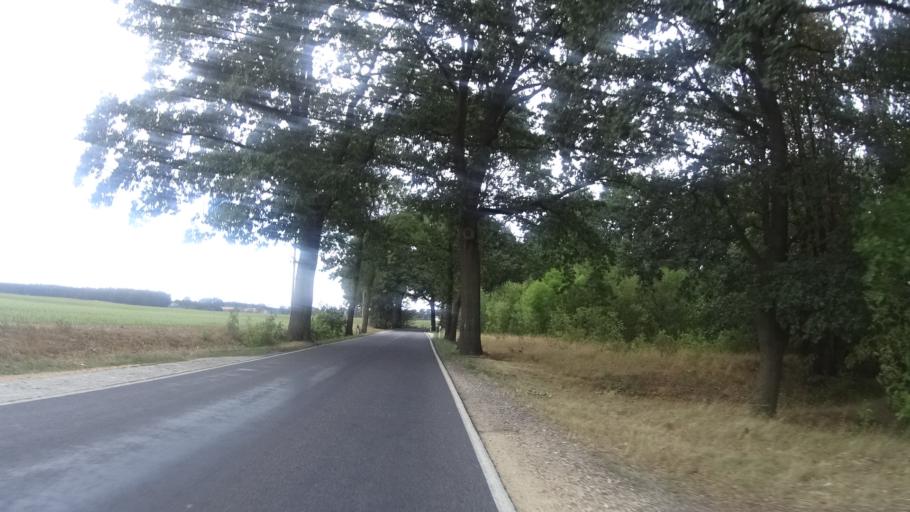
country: DE
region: Saxony
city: Rothenburg
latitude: 51.3040
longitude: 15.0057
